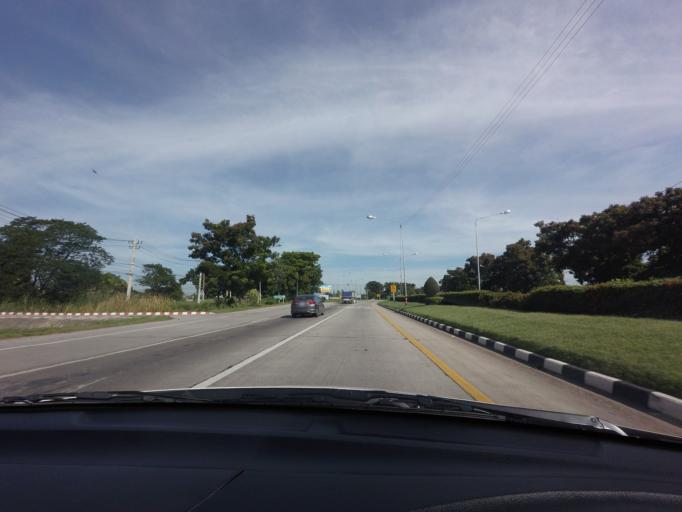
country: TH
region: Suphan Buri
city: Bang Pla Ma
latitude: 14.4052
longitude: 100.1580
